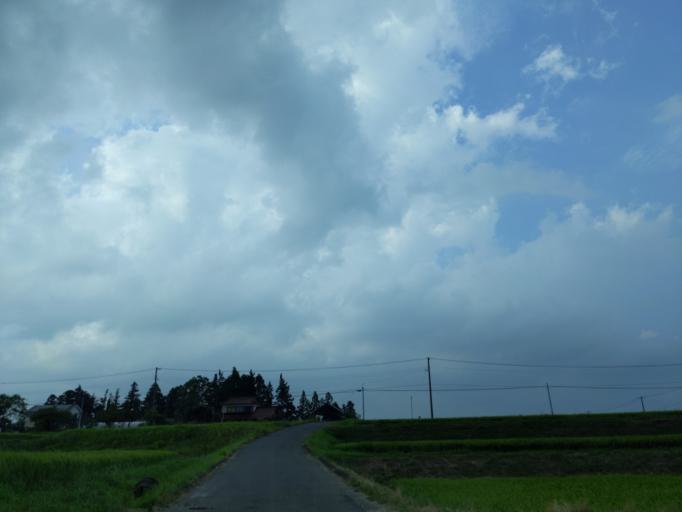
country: JP
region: Fukushima
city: Koriyama
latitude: 37.4388
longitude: 140.3664
